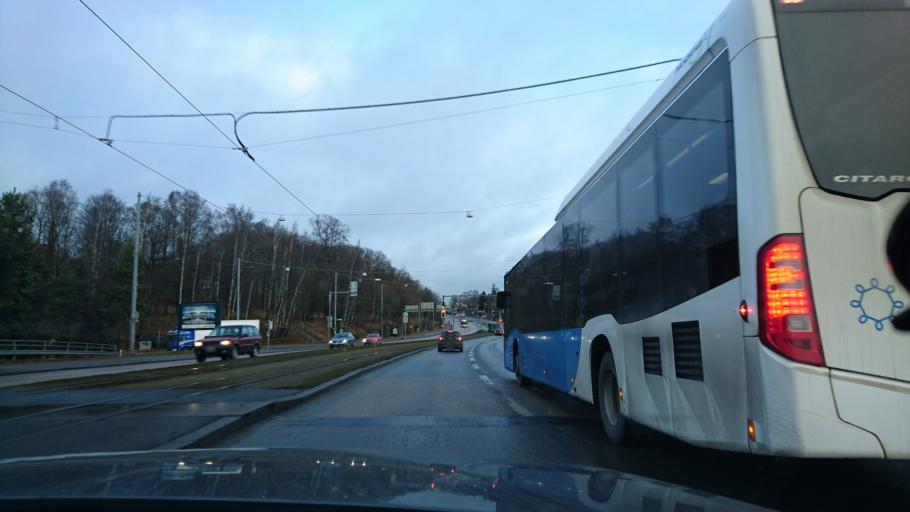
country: FI
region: Uusimaa
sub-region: Helsinki
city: Helsinki
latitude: 60.2013
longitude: 24.9630
